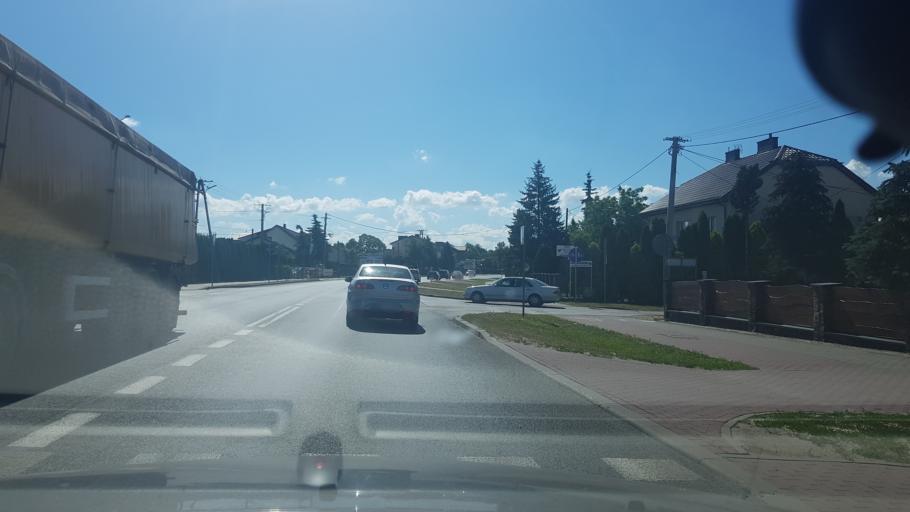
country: PL
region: Masovian Voivodeship
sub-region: Siedlce
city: Siedlce
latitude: 52.1978
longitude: 22.2614
